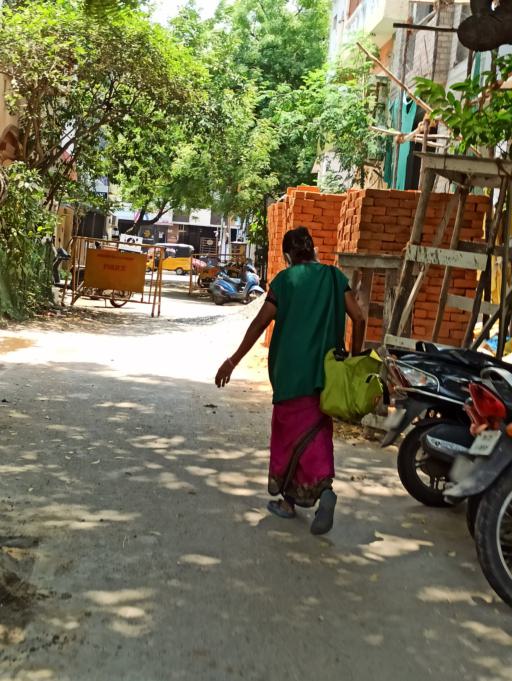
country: IN
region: Tamil Nadu
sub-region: Chennai
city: Chetput
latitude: 13.0642
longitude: 80.2313
